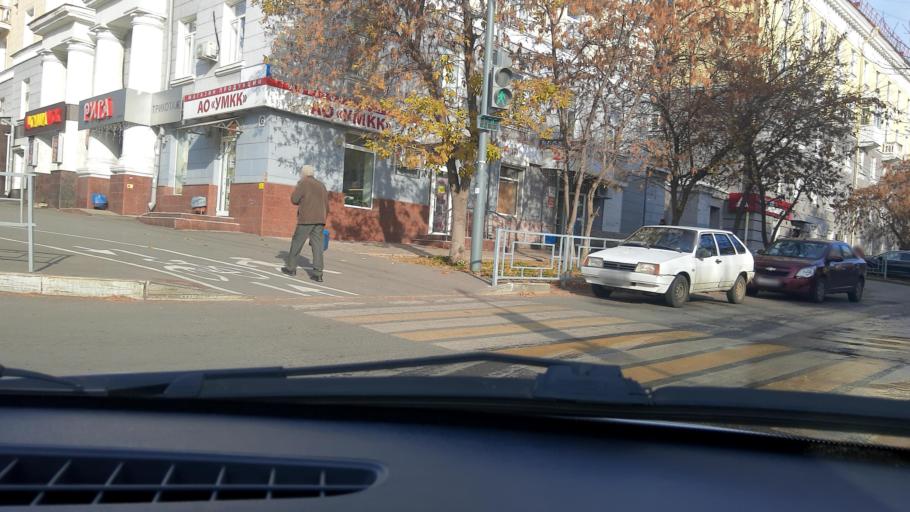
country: RU
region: Bashkortostan
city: Ufa
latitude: 54.8163
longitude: 56.0797
